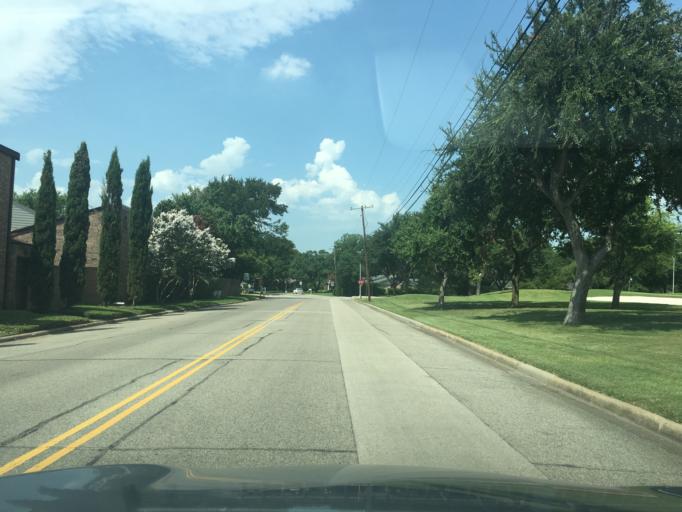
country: US
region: Texas
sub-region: Dallas County
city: Carrollton
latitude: 32.9339
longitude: -96.8640
